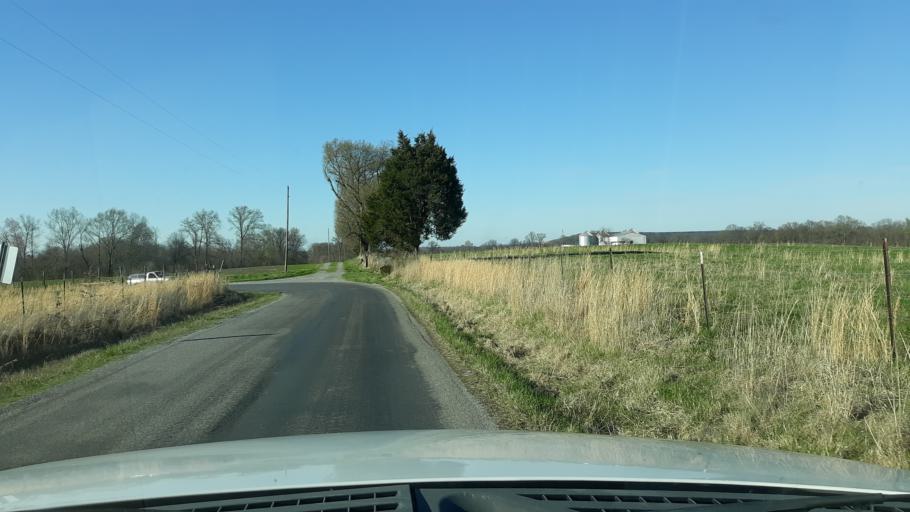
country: US
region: Illinois
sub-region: Saline County
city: Harrisburg
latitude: 37.7839
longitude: -88.6012
